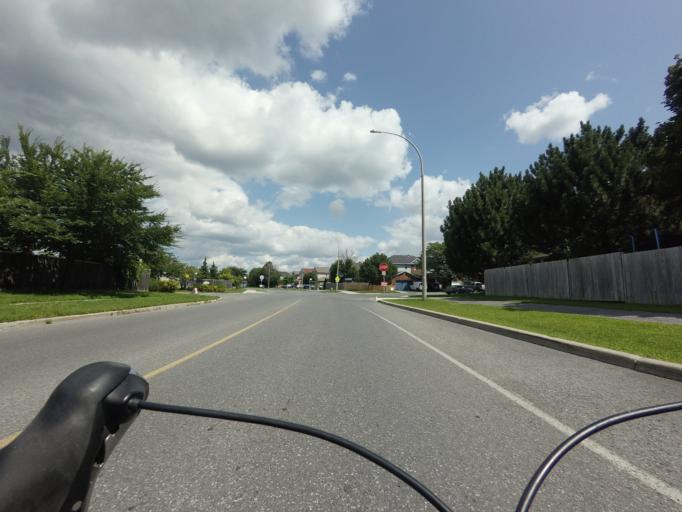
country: CA
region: Ontario
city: Bells Corners
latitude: 45.2788
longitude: -75.8565
